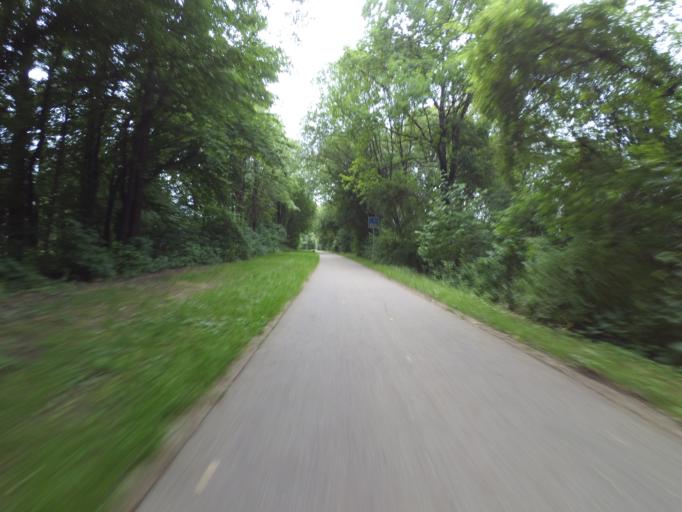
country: DE
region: North Rhine-Westphalia
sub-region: Regierungsbezirk Koln
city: Wurselen
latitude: 50.7687
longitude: 6.1621
